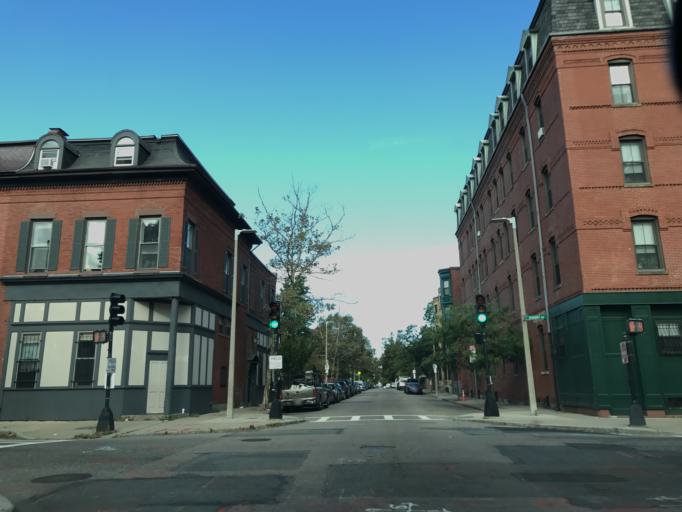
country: US
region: Massachusetts
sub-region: Suffolk County
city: Boston
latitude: 42.3368
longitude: -71.0786
